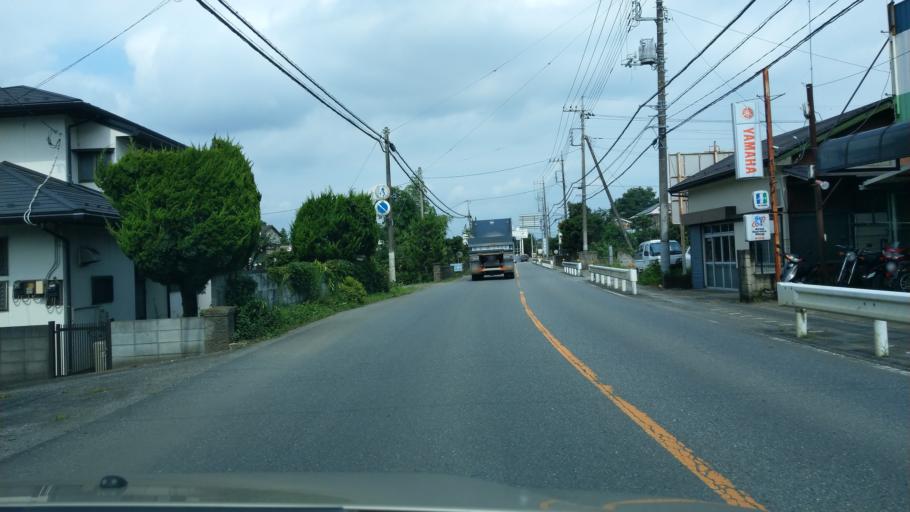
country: JP
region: Saitama
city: Ogawa
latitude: 36.0326
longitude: 139.3478
